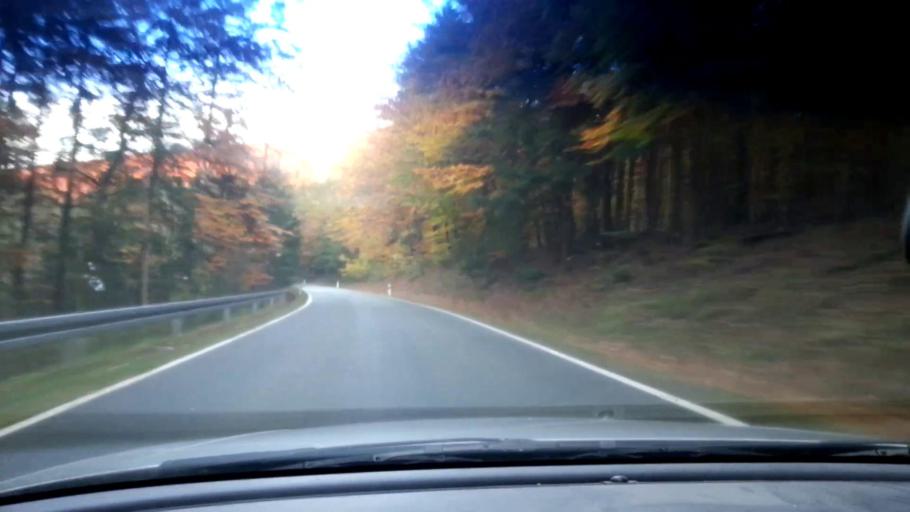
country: DE
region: Bavaria
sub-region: Upper Franconia
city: Heiligenstadt
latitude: 49.8634
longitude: 11.1271
